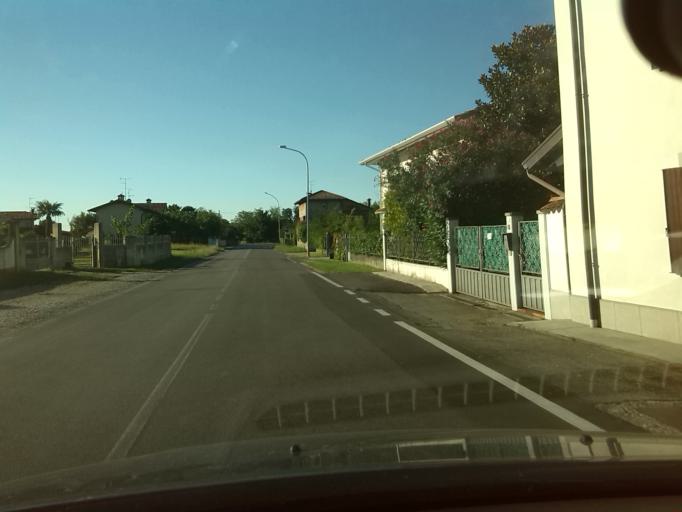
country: IT
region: Friuli Venezia Giulia
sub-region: Provincia di Udine
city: San Giovanni al Natisone
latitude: 45.9654
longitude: 13.4226
